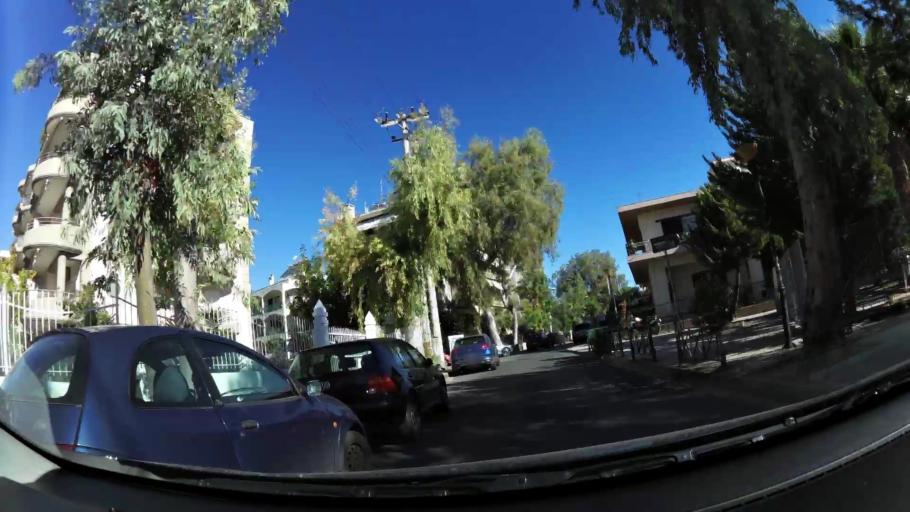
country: GR
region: Attica
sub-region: Nomarchia Athinas
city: Khalandrion
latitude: 38.0230
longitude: 23.8090
